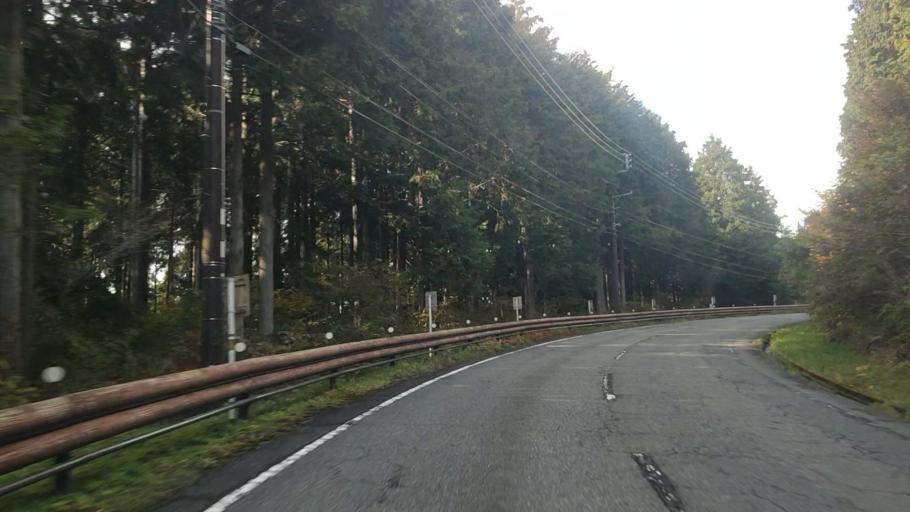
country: JP
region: Shizuoka
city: Fujinomiya
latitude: 35.2977
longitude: 138.6690
